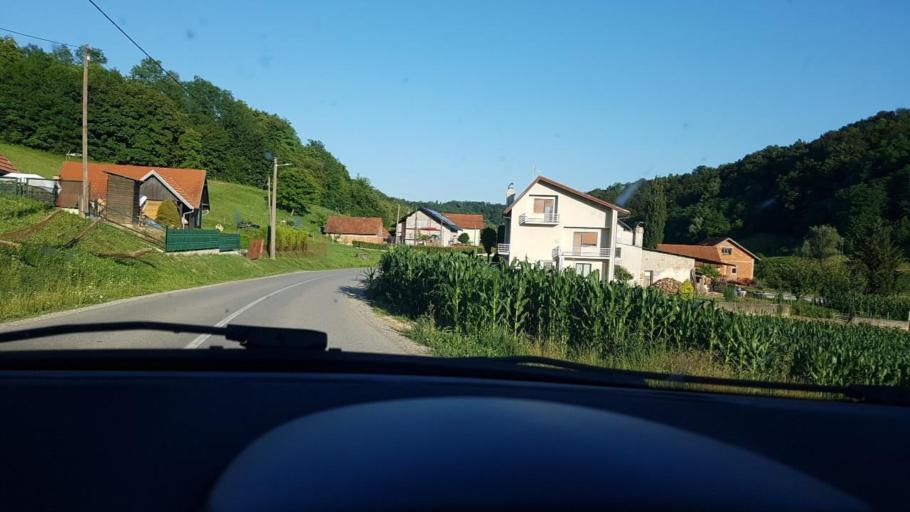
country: HR
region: Krapinsko-Zagorska
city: Bedekovcina
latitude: 46.0697
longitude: 15.9951
